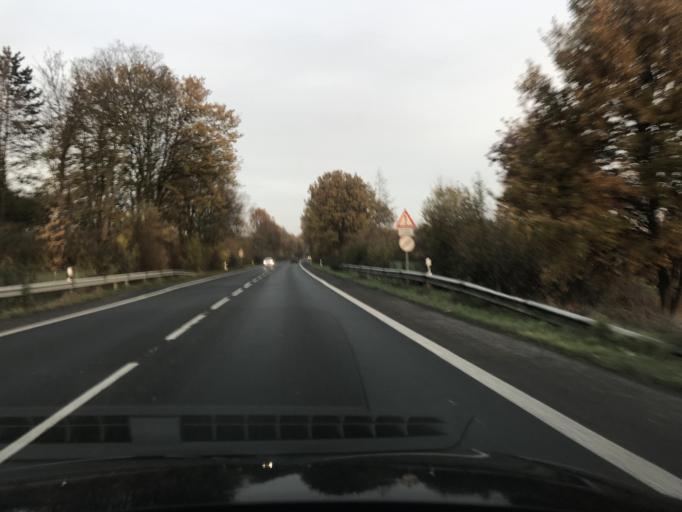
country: DE
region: North Rhine-Westphalia
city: Werne
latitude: 51.6988
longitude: 7.6757
